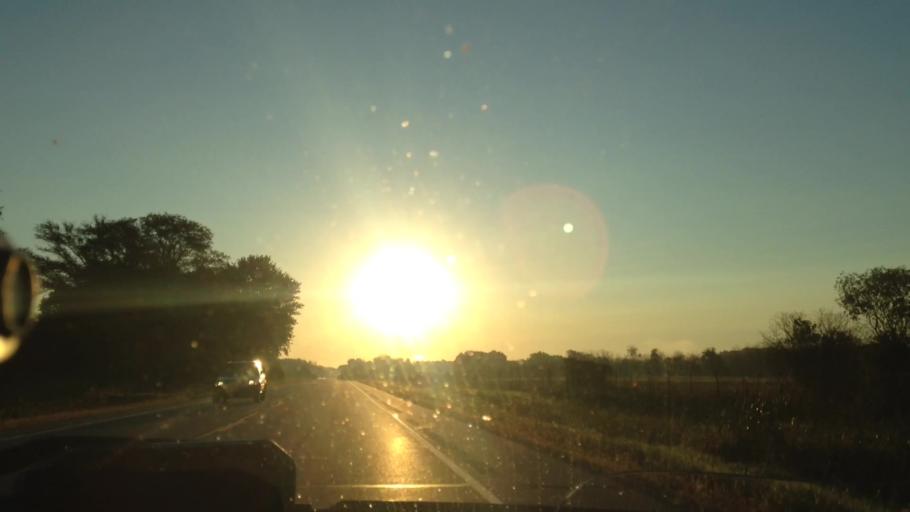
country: US
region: Wisconsin
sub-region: Washington County
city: West Bend
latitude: 43.4263
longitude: -88.1256
